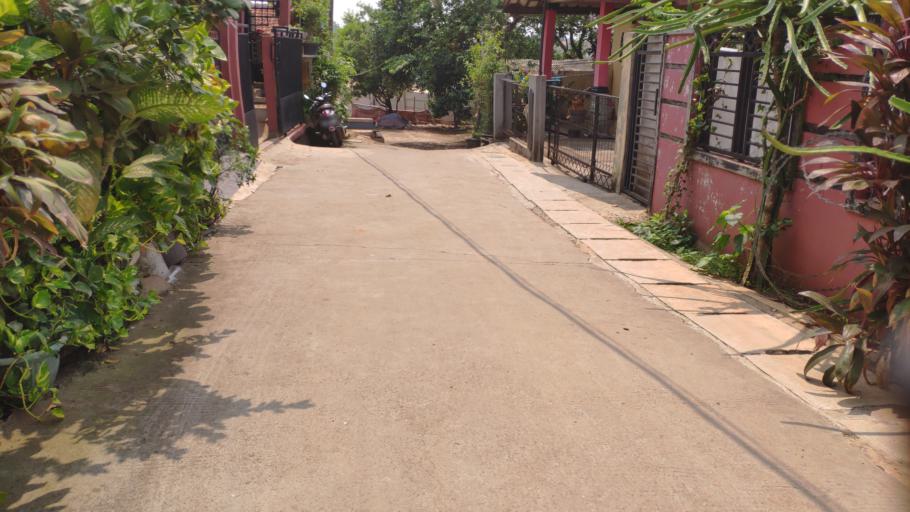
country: ID
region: West Java
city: Pamulang
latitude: -6.3448
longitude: 106.7952
